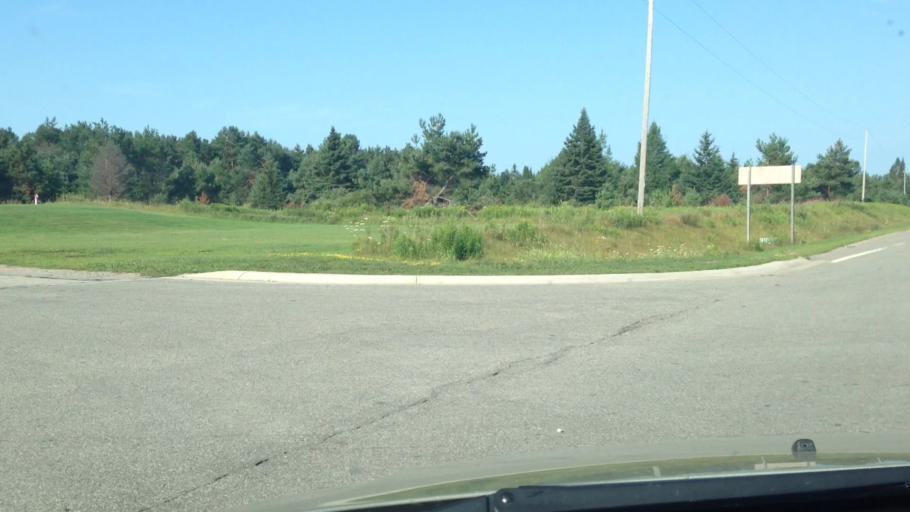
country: US
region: Michigan
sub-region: Schoolcraft County
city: Manistique
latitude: 46.1007
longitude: -85.9303
